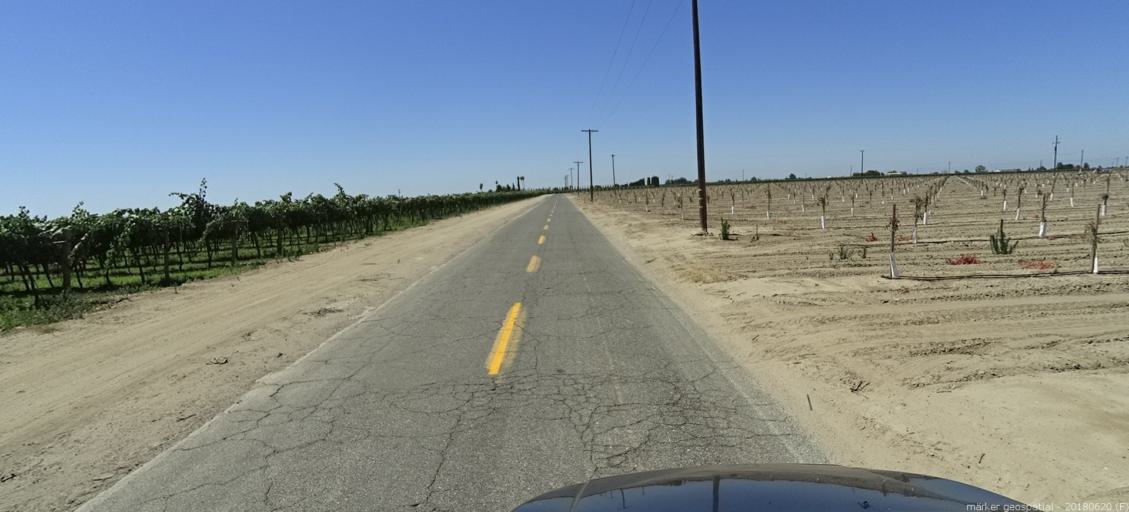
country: US
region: California
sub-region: Fresno County
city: Biola
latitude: 36.8405
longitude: -120.0010
